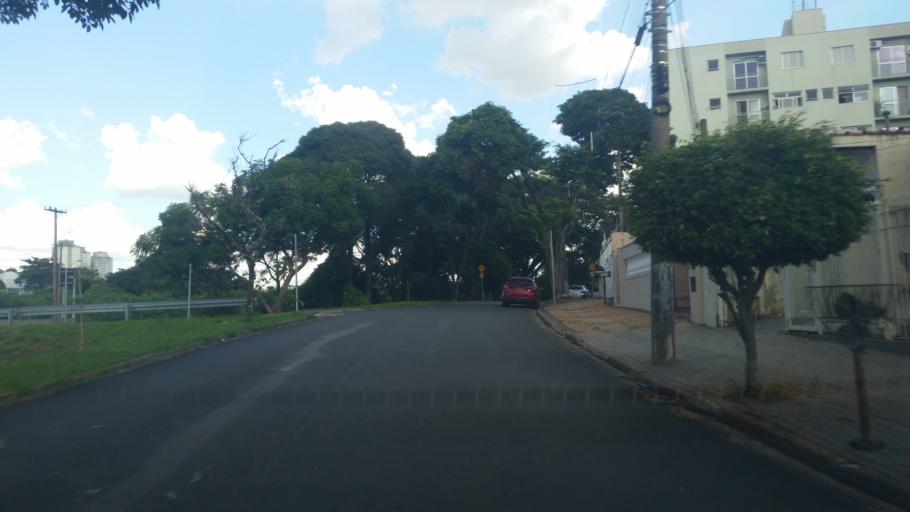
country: BR
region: Sao Paulo
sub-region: Campinas
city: Campinas
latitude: -22.8795
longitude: -47.0325
